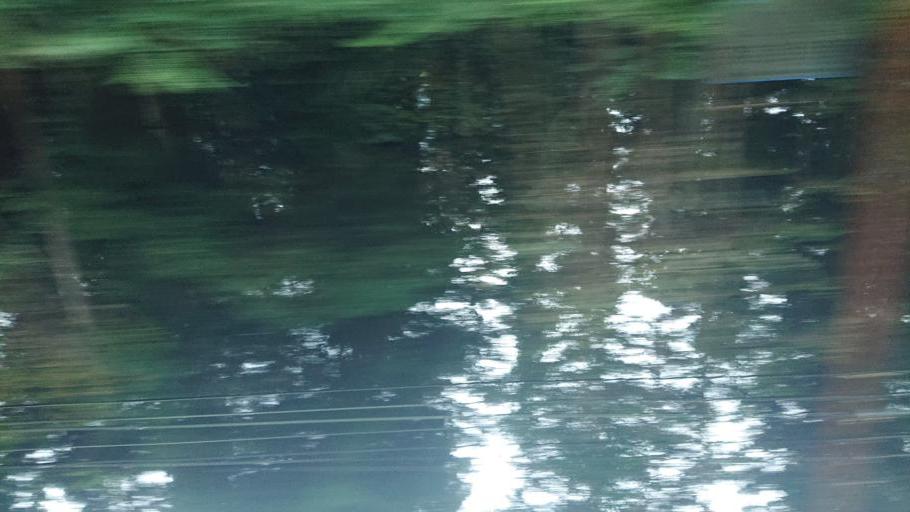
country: TW
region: Taiwan
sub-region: Chiayi
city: Jiayi Shi
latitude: 23.4766
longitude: 120.7190
